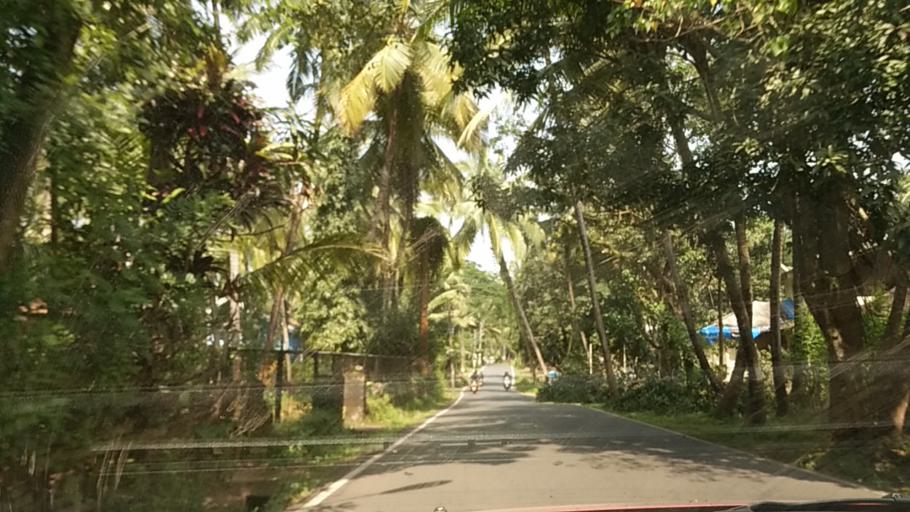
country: IN
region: Goa
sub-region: South Goa
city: Colva
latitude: 15.2929
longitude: 73.9206
